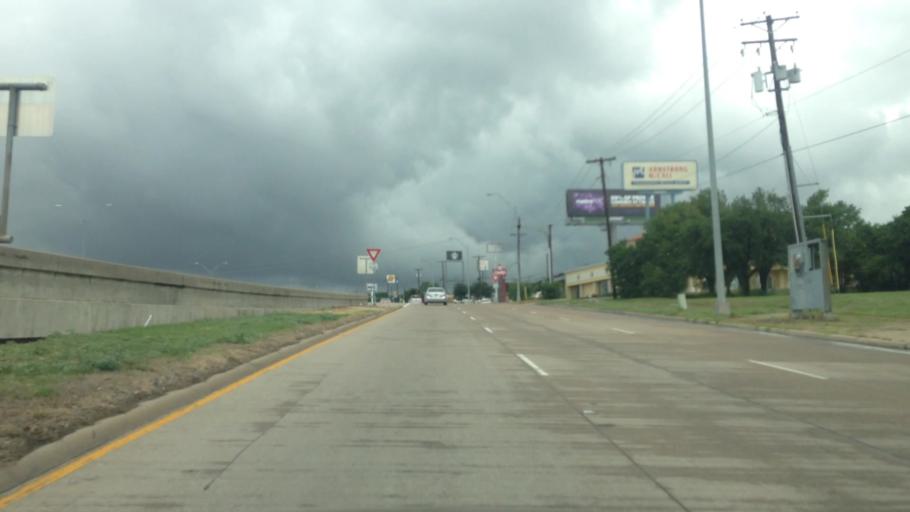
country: US
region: Texas
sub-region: Tarrant County
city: Edgecliff Village
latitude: 32.6736
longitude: -97.3787
